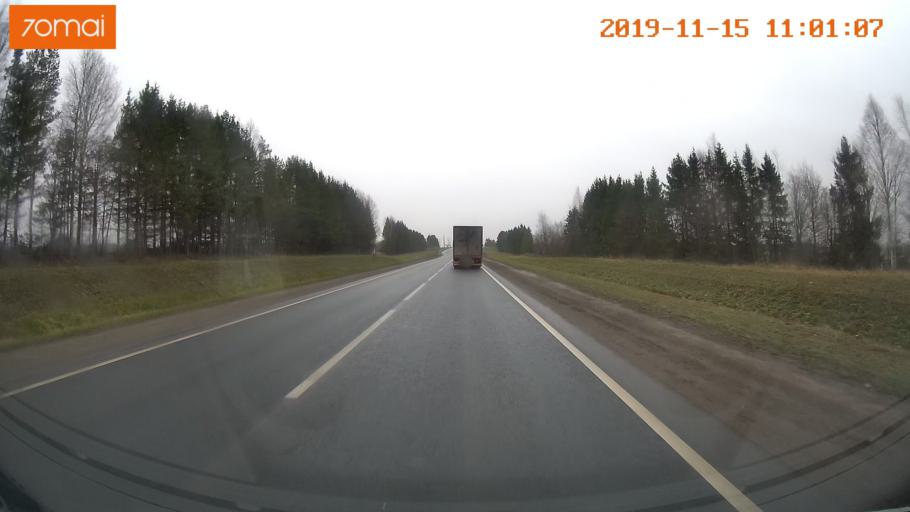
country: RU
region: Vologda
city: Chebsara
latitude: 59.1342
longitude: 38.9137
